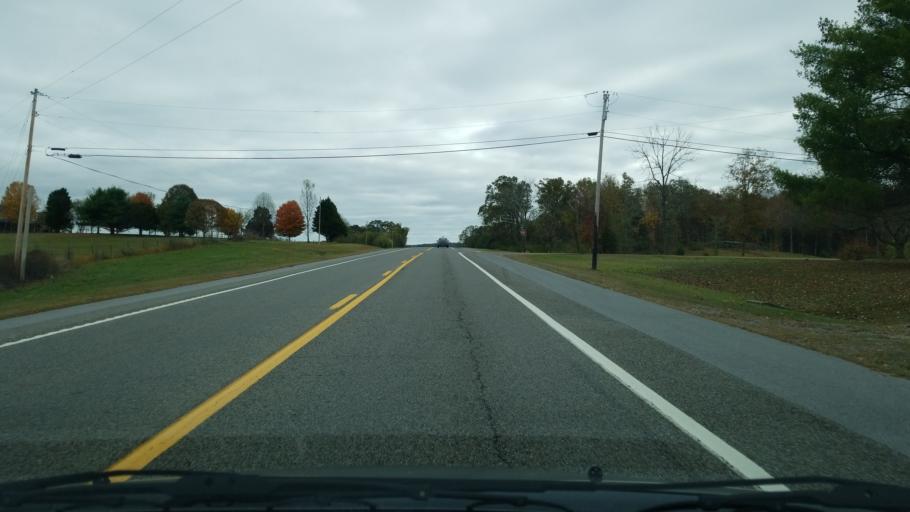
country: US
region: Tennessee
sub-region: Rhea County
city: Graysville
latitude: 35.3905
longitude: -85.0069
